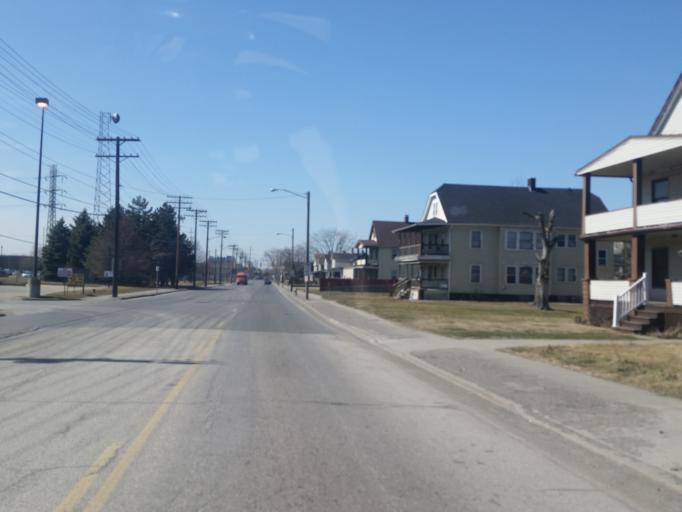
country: US
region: Ohio
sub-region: Cuyahoga County
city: Newburgh Heights
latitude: 41.4470
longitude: -81.6585
